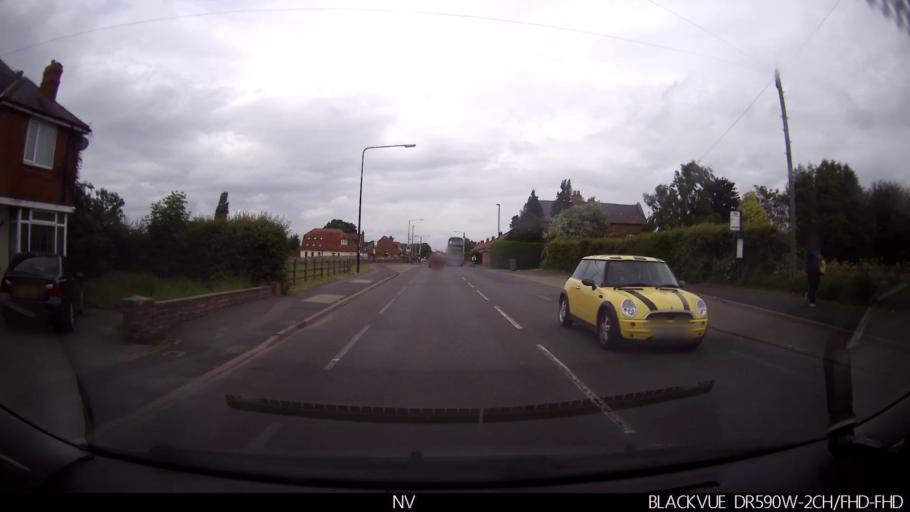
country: GB
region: England
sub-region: City of York
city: Haxby
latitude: 54.0025
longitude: -1.0731
